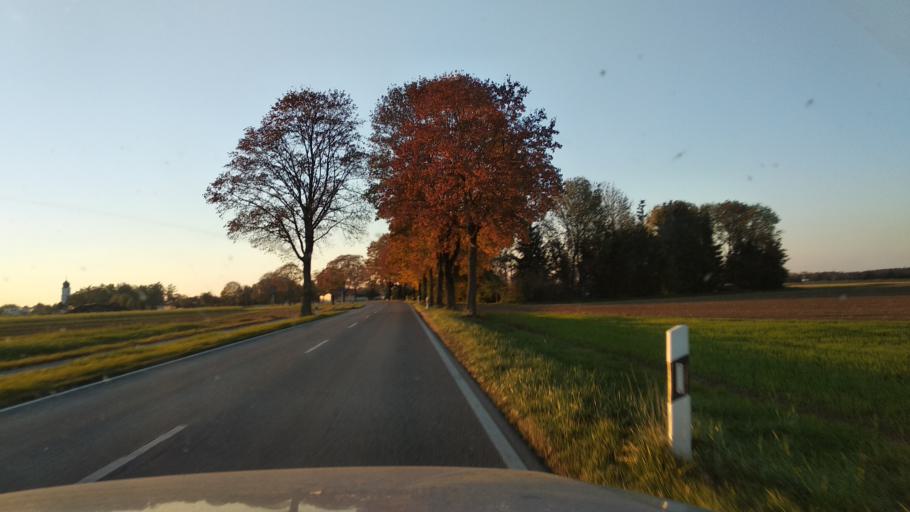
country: DE
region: Bavaria
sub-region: Upper Bavaria
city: Hohenkirchen-Siegertsbrunn
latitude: 48.0166
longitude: 11.7406
